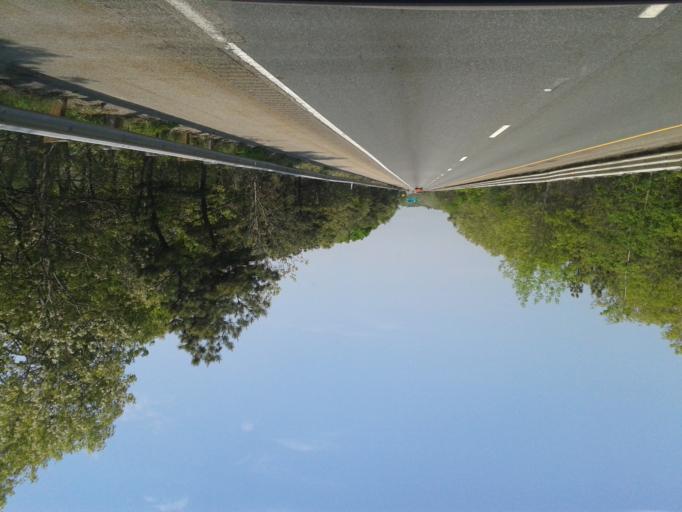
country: US
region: Massachusetts
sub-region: Barnstable County
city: Sagamore
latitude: 41.8108
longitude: -70.5518
